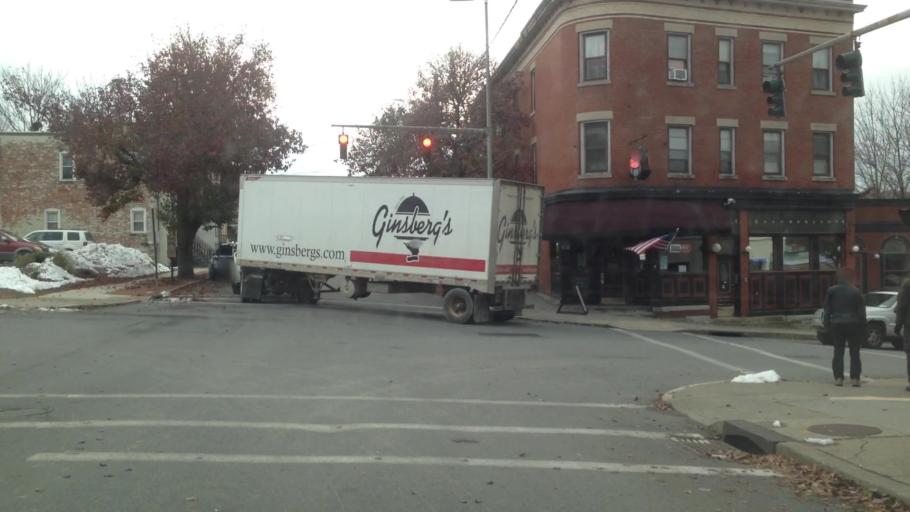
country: US
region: New York
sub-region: Dutchess County
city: Poughkeepsie
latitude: 41.7059
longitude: -73.9355
